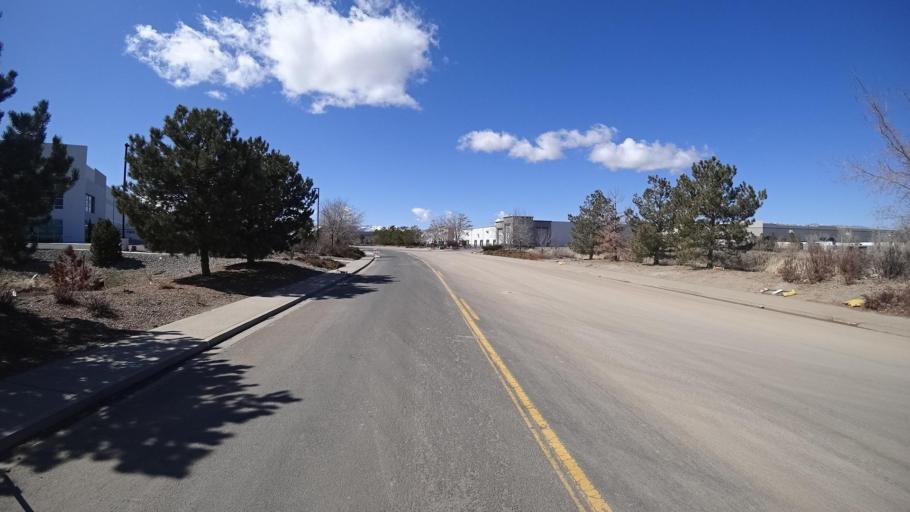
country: US
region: Nevada
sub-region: Washoe County
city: Lemmon Valley
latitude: 39.6468
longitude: -119.8576
